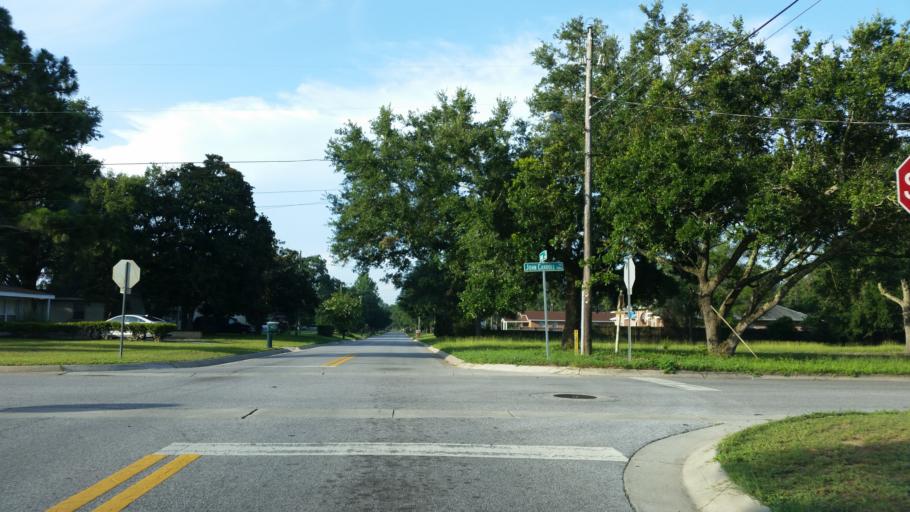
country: US
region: Florida
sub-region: Escambia County
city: Ferry Pass
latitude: 30.4919
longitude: -87.2009
